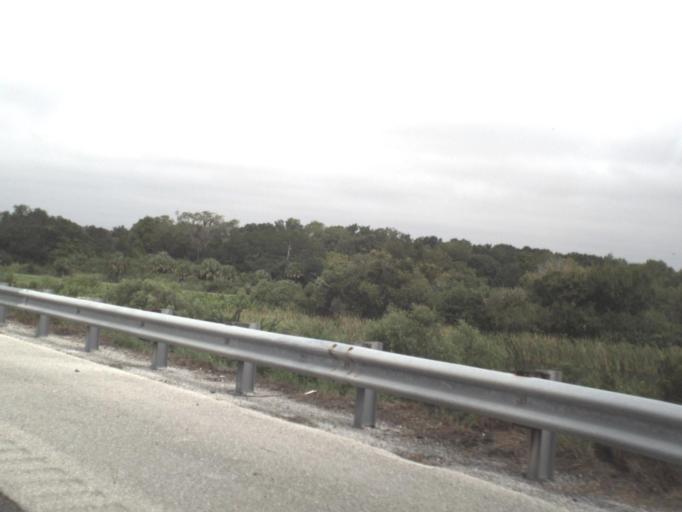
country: US
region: Florida
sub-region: Manatee County
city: Ellenton
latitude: 27.5856
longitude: -82.5173
